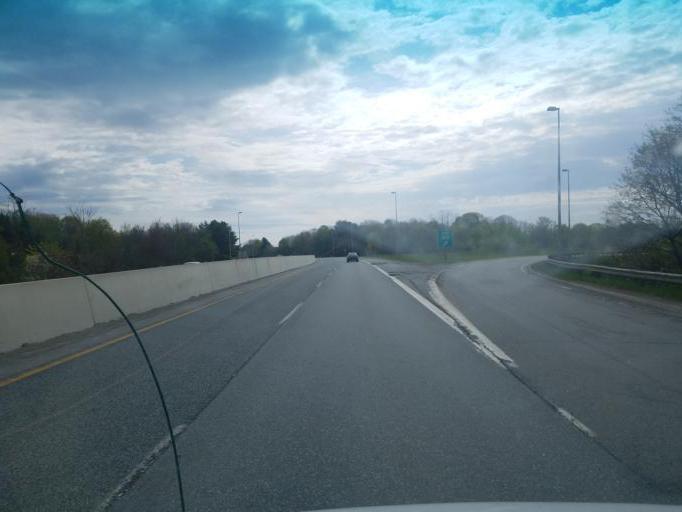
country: US
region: Maine
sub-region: Penobscot County
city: Bangor
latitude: 44.8190
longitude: -68.7746
